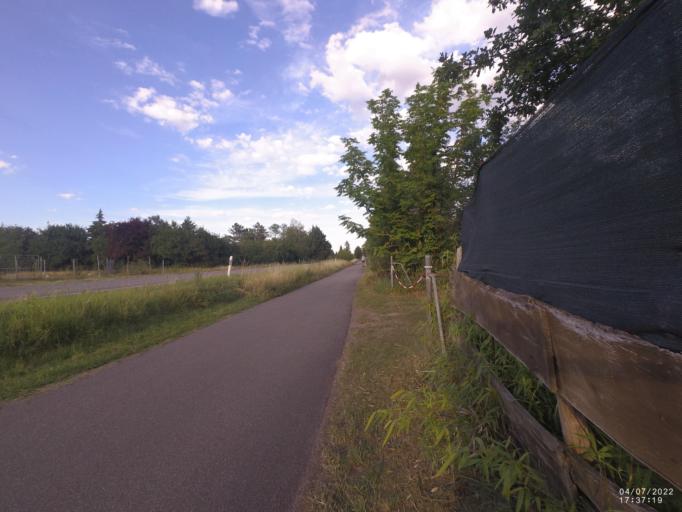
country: DE
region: Rheinland-Pfalz
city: Hassloch
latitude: 49.3633
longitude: 8.2220
